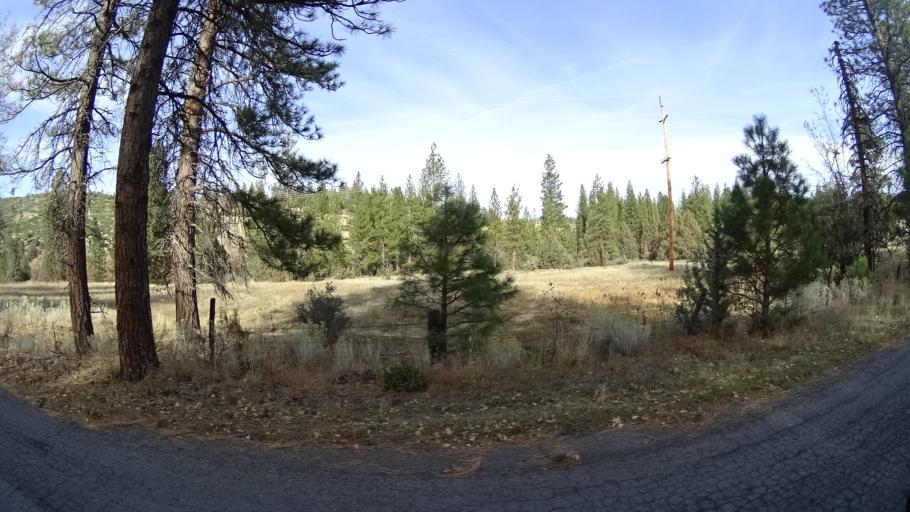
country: US
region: California
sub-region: Siskiyou County
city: Weed
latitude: 41.4666
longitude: -122.4063
